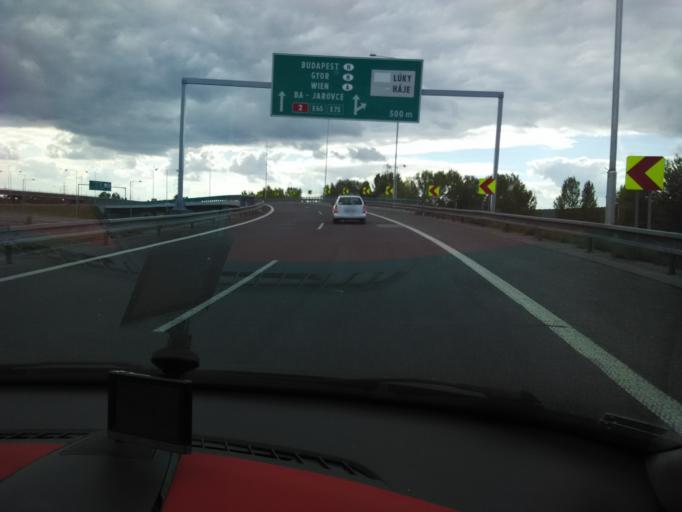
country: AT
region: Burgenland
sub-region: Politischer Bezirk Neusiedl am See
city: Kittsee
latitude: 48.1266
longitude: 17.0764
